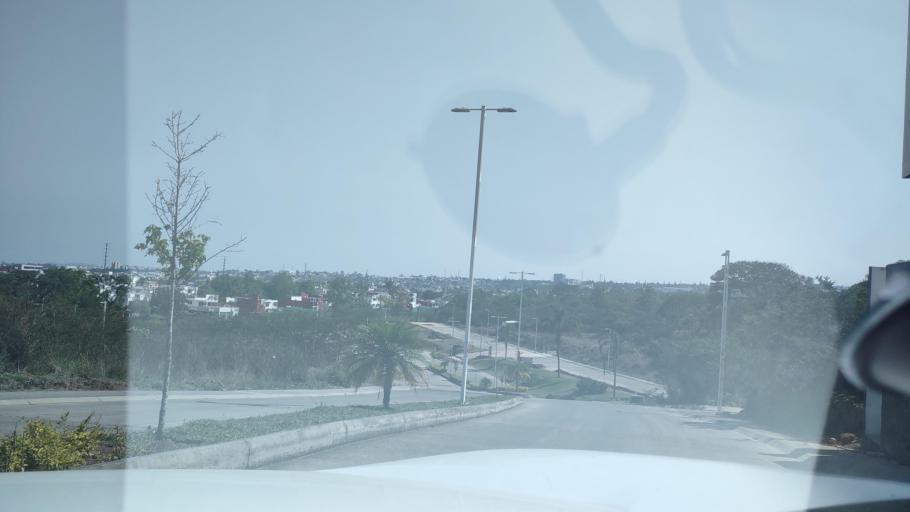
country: MX
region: Veracruz
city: El Castillo
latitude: 19.5280
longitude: -96.8695
